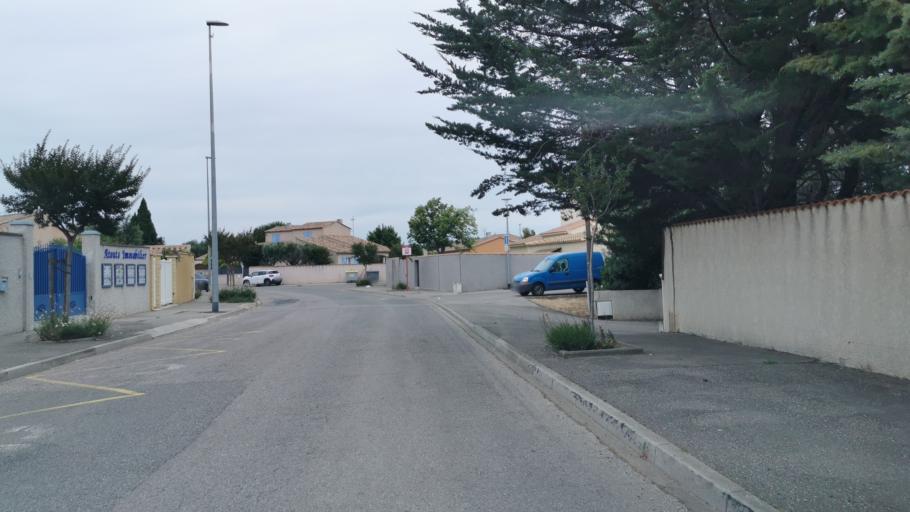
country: FR
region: Languedoc-Roussillon
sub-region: Departement de l'Aude
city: Narbonne
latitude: 43.1954
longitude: 3.0218
